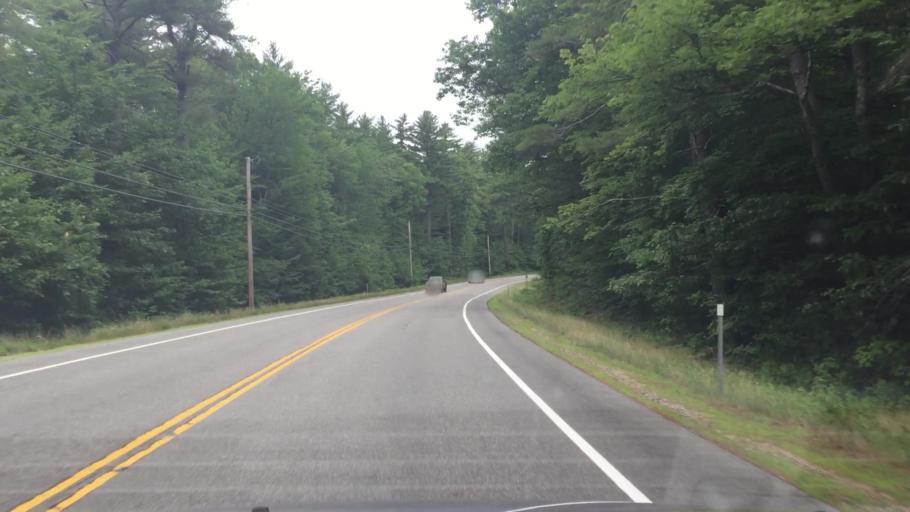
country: US
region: New Hampshire
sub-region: Carroll County
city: Sandwich
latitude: 43.8168
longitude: -71.3534
